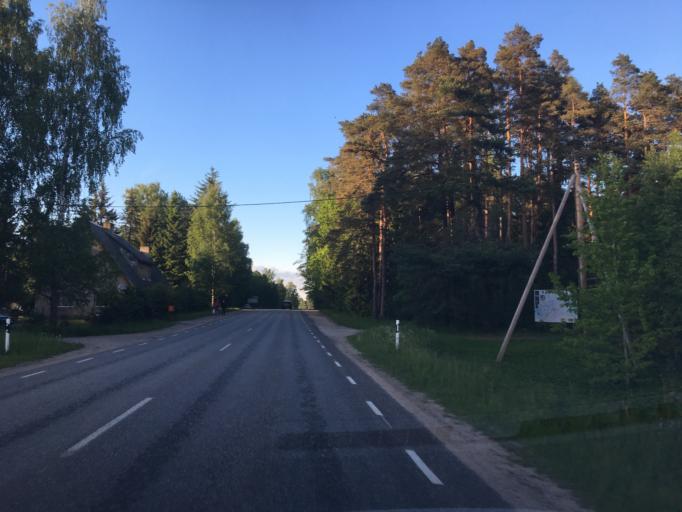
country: EE
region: Tartu
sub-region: Noo vald
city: Noo
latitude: 58.1997
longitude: 26.5699
